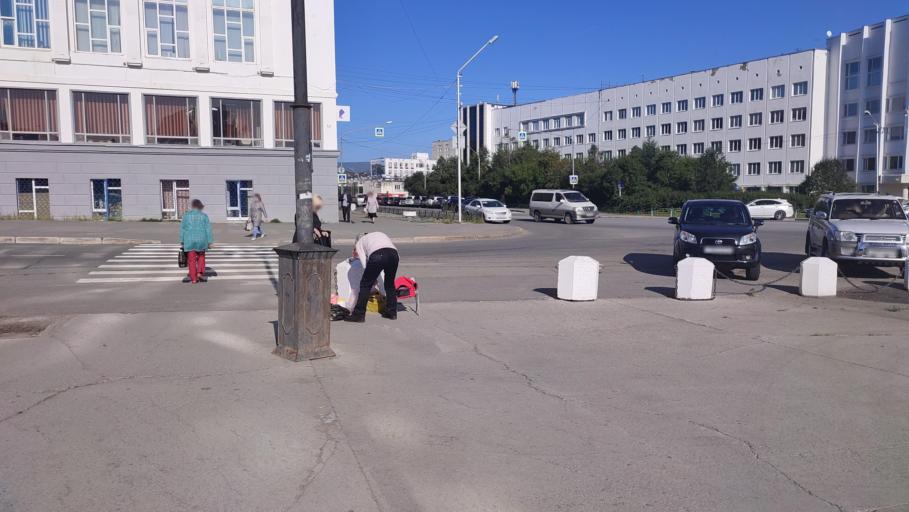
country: RU
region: Magadan
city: Magadan
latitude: 59.5666
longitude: 150.8111
